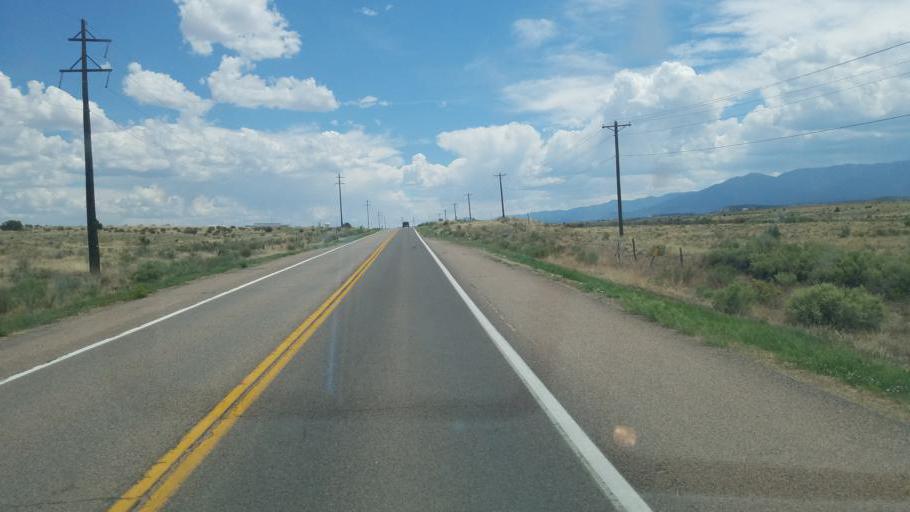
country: US
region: Colorado
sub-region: Fremont County
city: Florence
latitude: 38.3736
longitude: -105.1094
